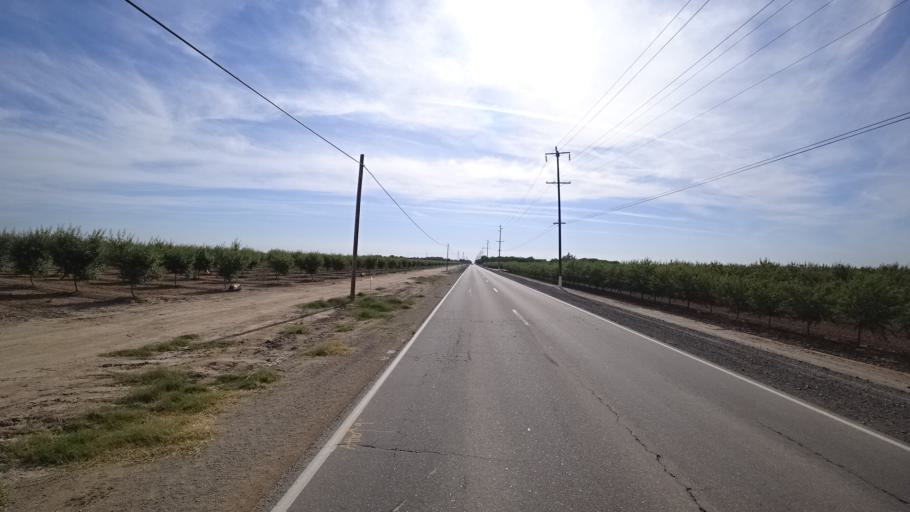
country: US
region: California
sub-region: Kings County
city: Hanford
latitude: 36.3426
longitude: -119.5901
